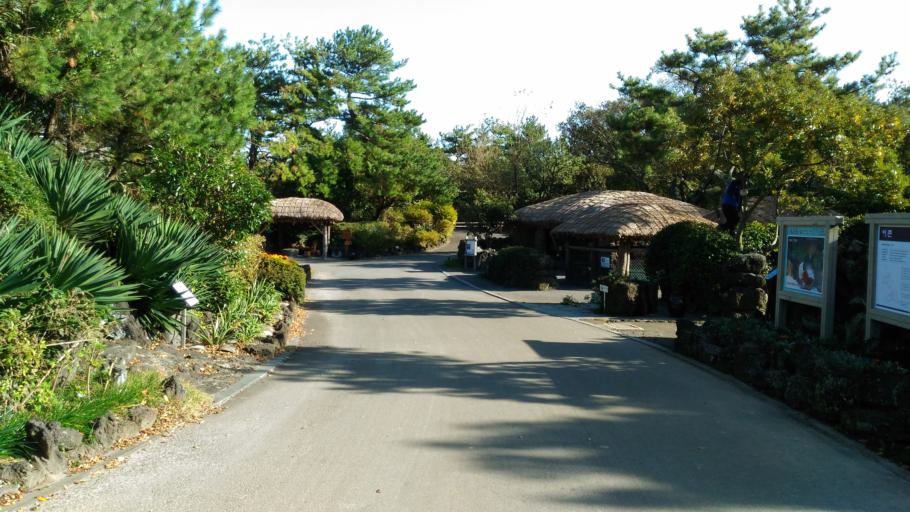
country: KR
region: Jeju-do
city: Seogwipo
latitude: 33.3215
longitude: 126.8409
